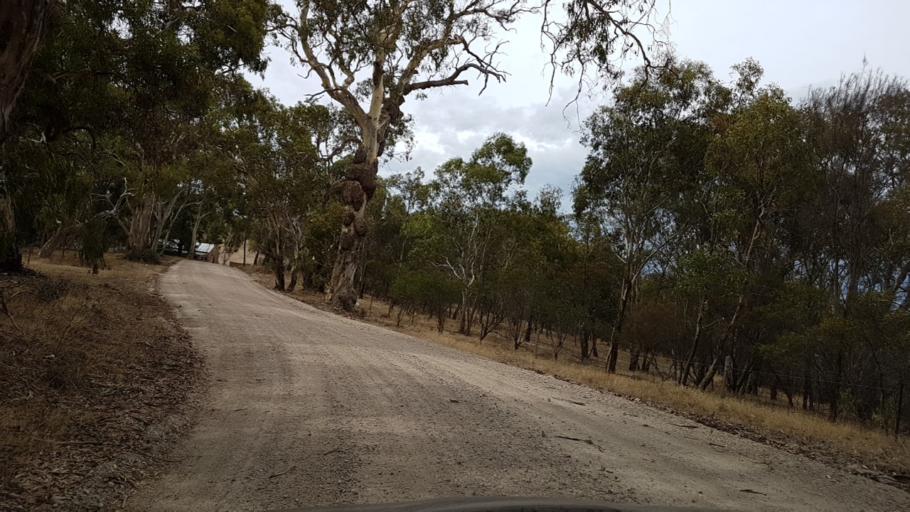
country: AU
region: South Australia
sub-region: Adelaide Hills
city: Birdwood
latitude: -34.7674
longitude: 138.9920
